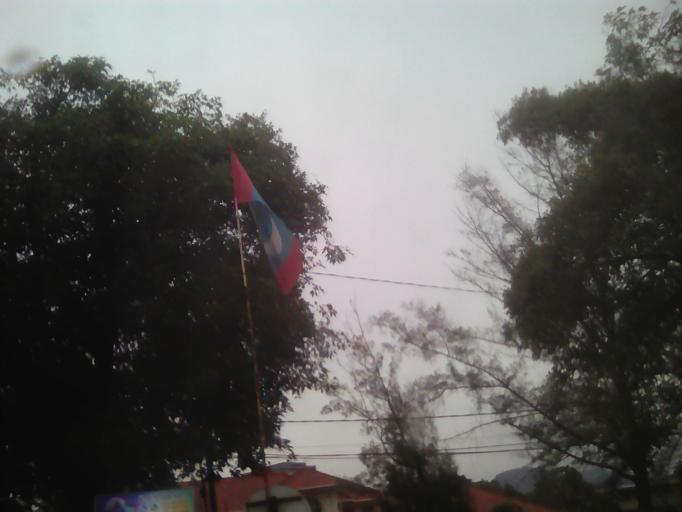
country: MY
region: Kedah
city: Kulim
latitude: 5.3707
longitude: 100.5579
